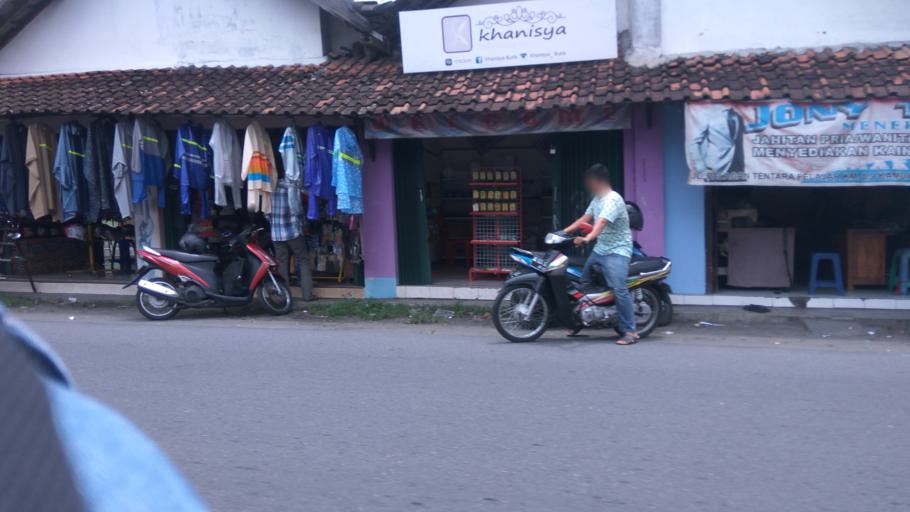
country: ID
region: Daerah Istimewa Yogyakarta
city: Melati
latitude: -7.7204
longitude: 110.3830
